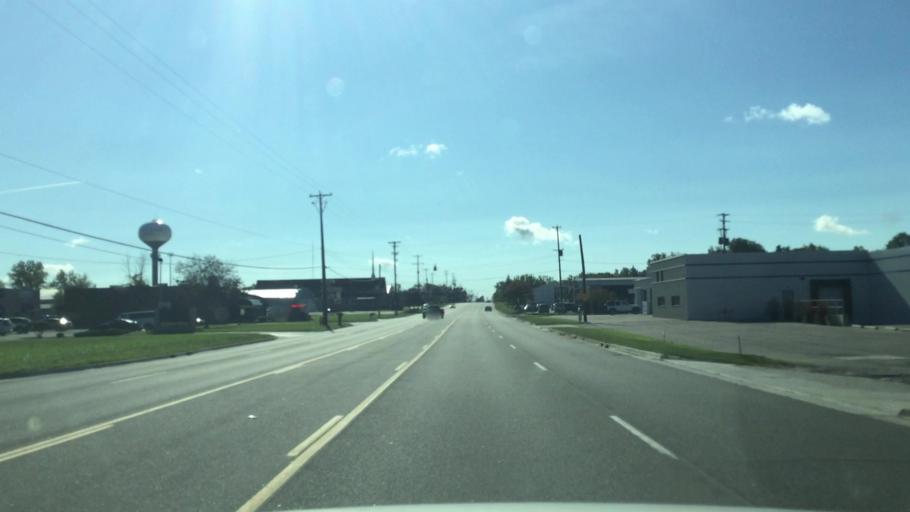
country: US
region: Michigan
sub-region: Genesee County
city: Grand Blanc
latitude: 42.9555
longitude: -83.6623
